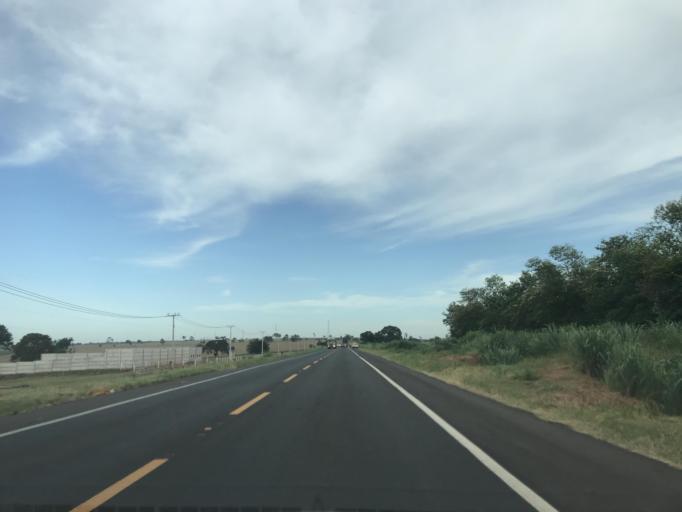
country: BR
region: Parana
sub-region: Paranavai
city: Paranavai
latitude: -23.0146
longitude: -52.5212
